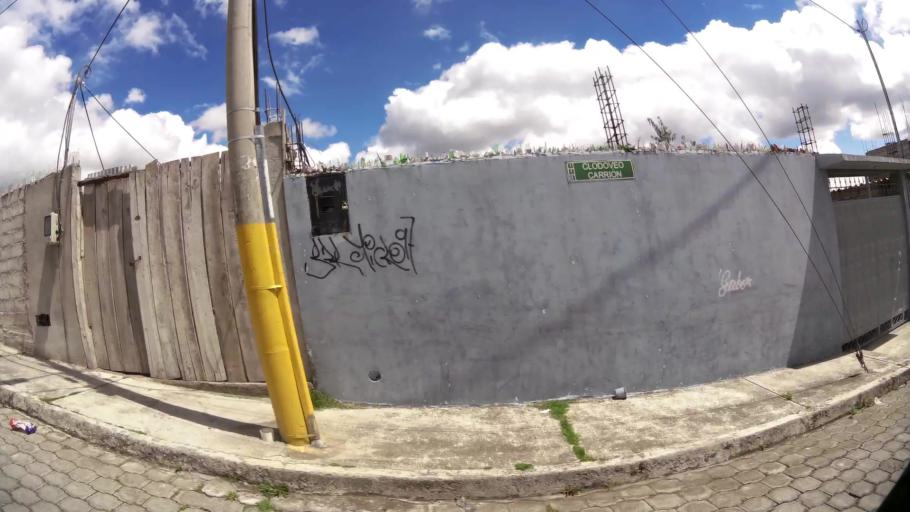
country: EC
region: Pichincha
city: Quito
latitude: -0.3340
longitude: -78.5646
